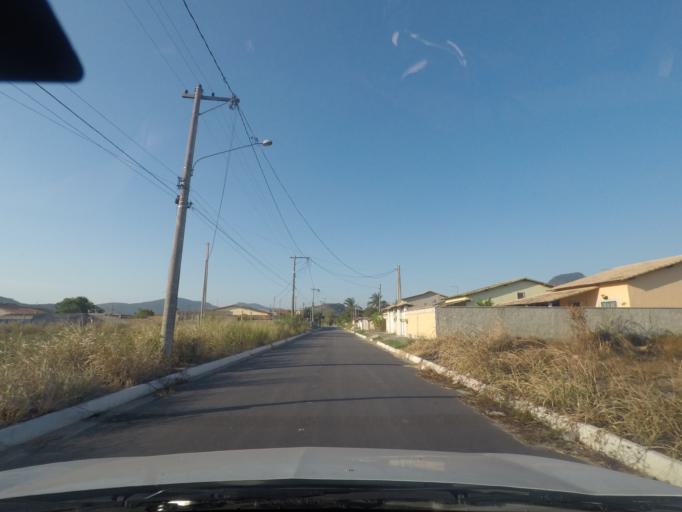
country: BR
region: Rio de Janeiro
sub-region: Marica
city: Marica
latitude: -22.9579
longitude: -42.9352
